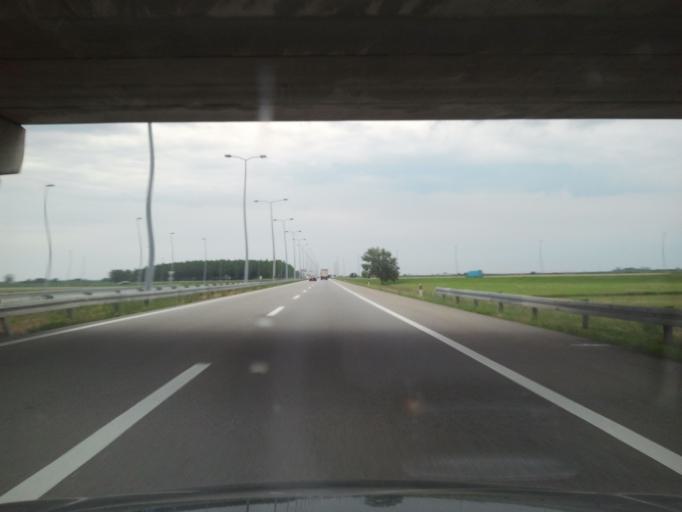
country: RS
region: Autonomna Pokrajina Vojvodina
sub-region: Sremski Okrug
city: Sremska Mitrovica
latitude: 44.9989
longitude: 19.6505
